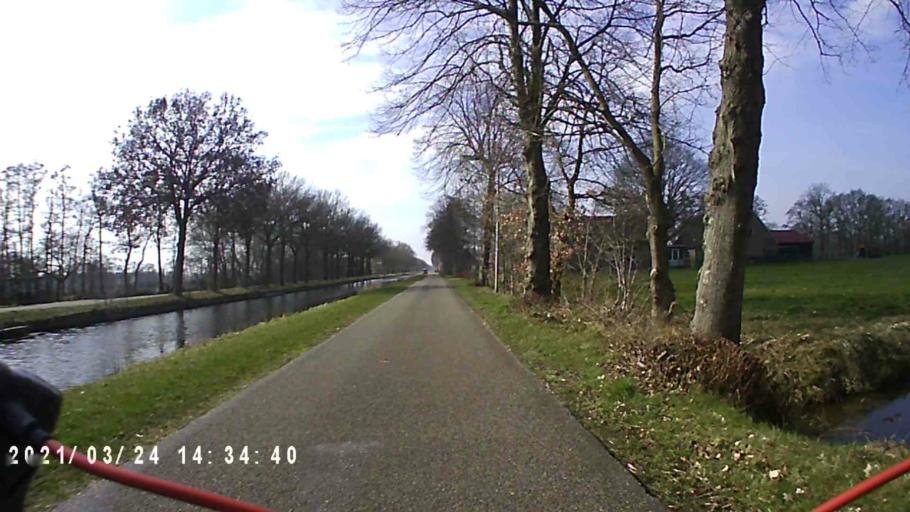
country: NL
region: Friesland
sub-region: Gemeente Heerenveen
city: Jubbega
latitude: 53.0303
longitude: 6.1575
